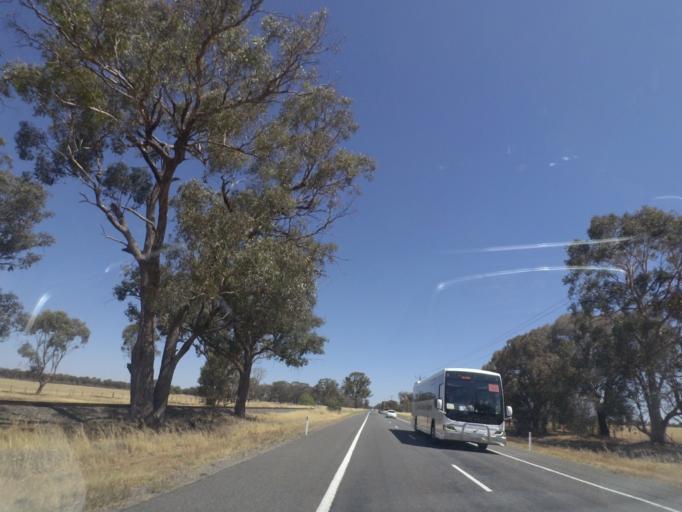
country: AU
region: Victoria
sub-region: Greater Shepparton
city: Shepparton
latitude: -36.2073
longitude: 145.4319
